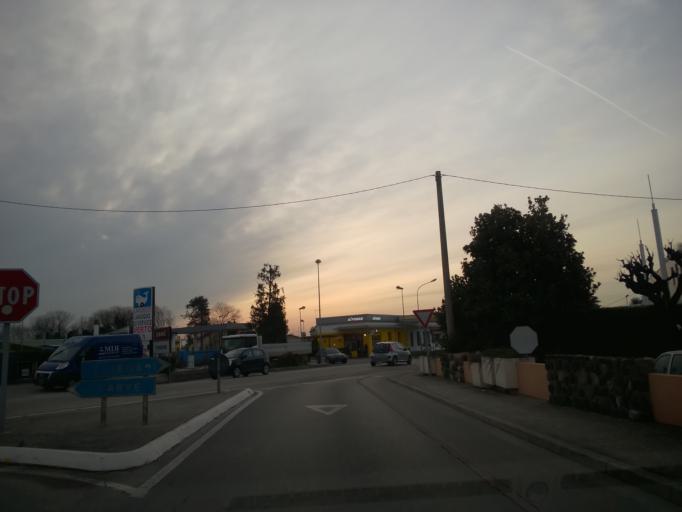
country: IT
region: Veneto
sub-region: Provincia di Vicenza
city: Thiene
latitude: 45.7167
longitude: 11.4705
